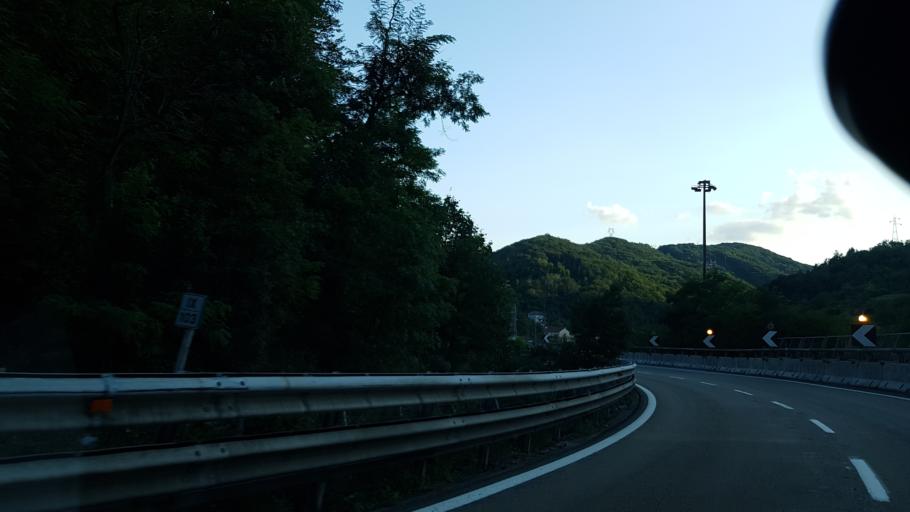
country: IT
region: Liguria
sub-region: Provincia di Genova
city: Ronco Scrivia
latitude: 44.6197
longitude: 8.9476
